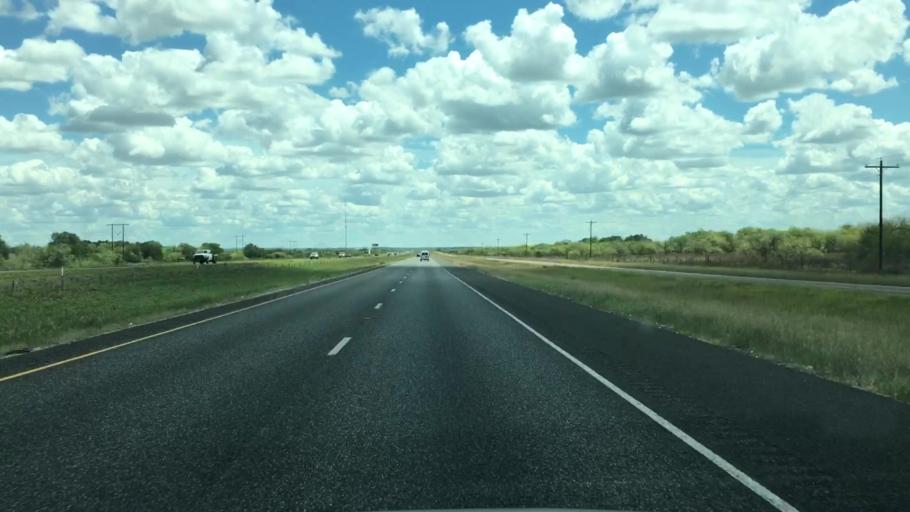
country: US
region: Texas
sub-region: Atascosa County
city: Pleasanton
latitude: 28.8133
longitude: -98.3547
